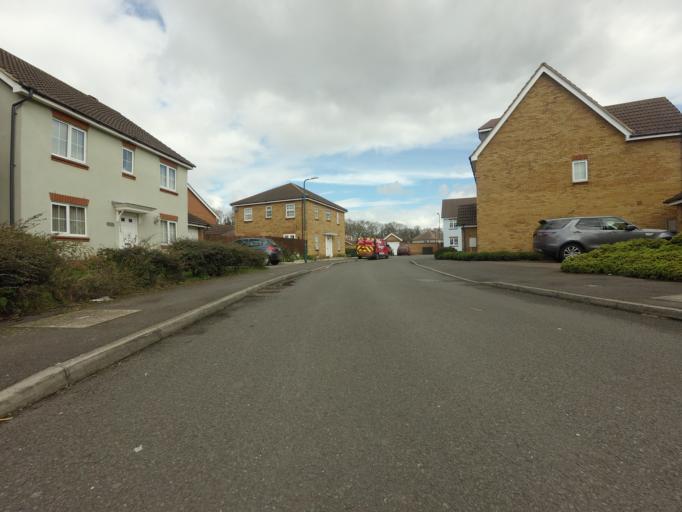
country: GB
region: England
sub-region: Kent
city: Swanley
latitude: 51.3963
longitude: 0.1844
